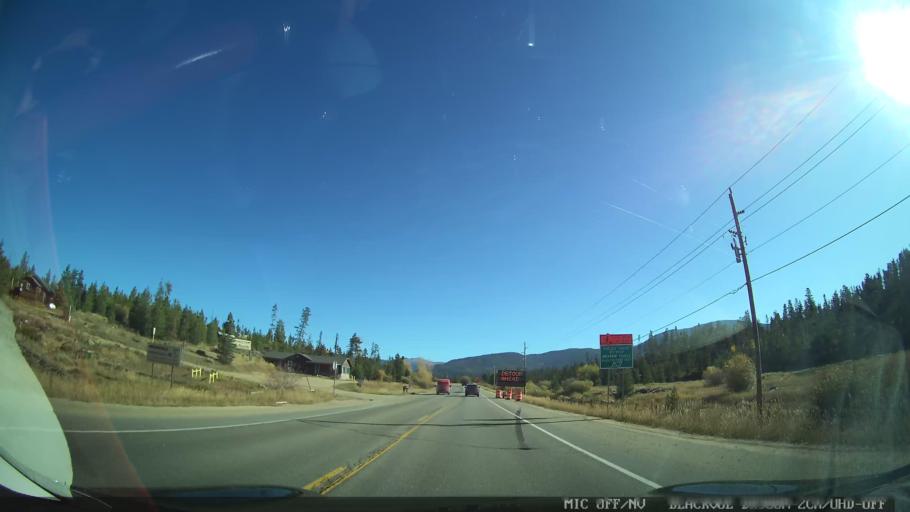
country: US
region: Colorado
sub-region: Grand County
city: Granby
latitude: 40.2014
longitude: -105.8646
